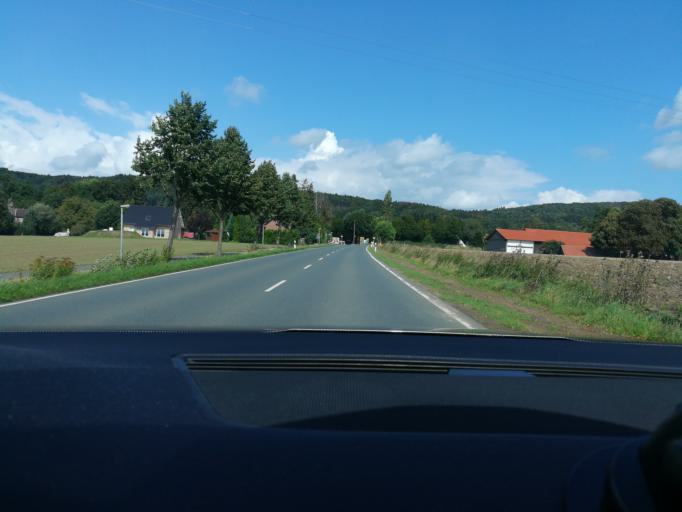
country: DE
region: North Rhine-Westphalia
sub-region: Regierungsbezirk Detmold
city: Huellhorst
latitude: 52.2863
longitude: 8.6660
